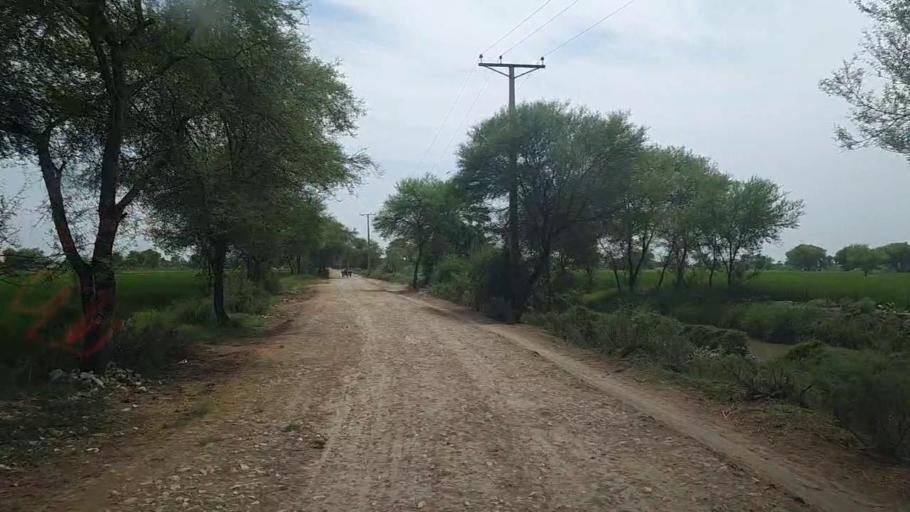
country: PK
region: Sindh
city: Thul
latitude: 28.2547
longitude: 68.6978
